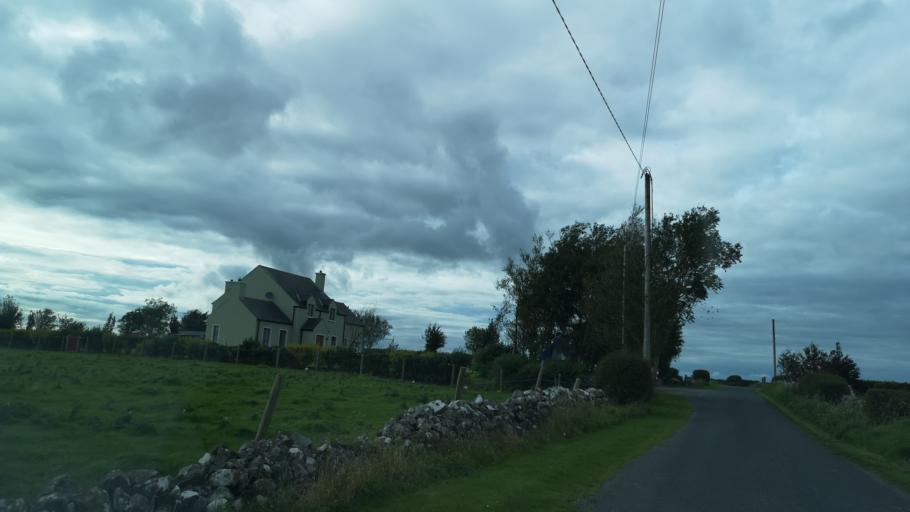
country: IE
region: Connaught
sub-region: County Galway
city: Ballinasloe
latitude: 53.3703
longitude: -8.1637
